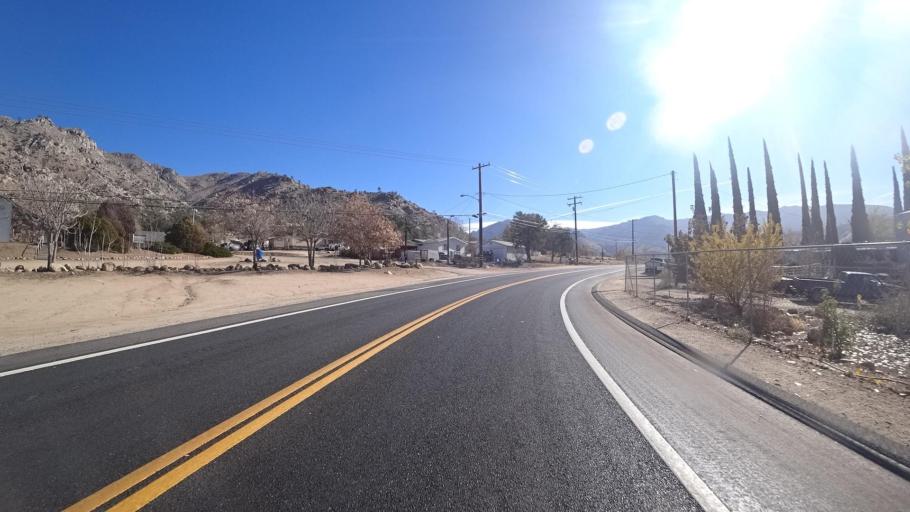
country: US
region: California
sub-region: Kern County
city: Lake Isabella
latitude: 35.6159
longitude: -118.4676
